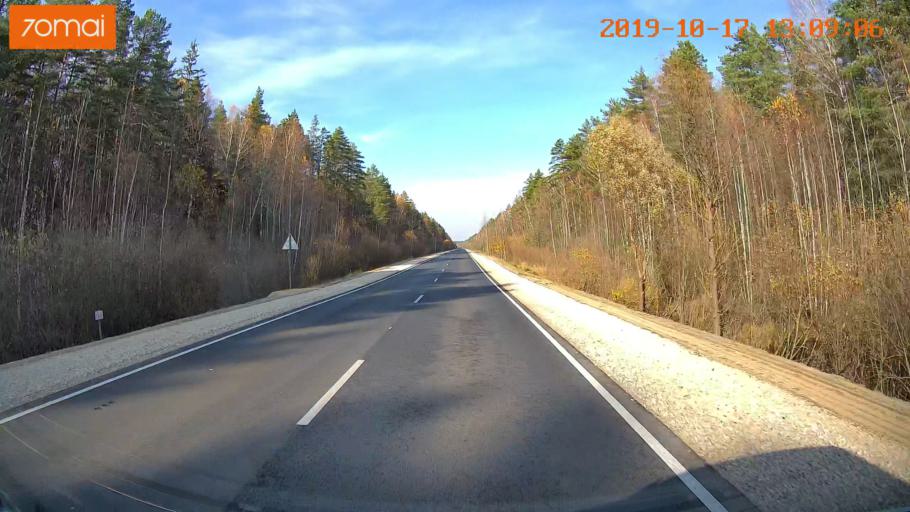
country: RU
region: Rjazan
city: Syntul
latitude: 54.9988
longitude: 41.2651
